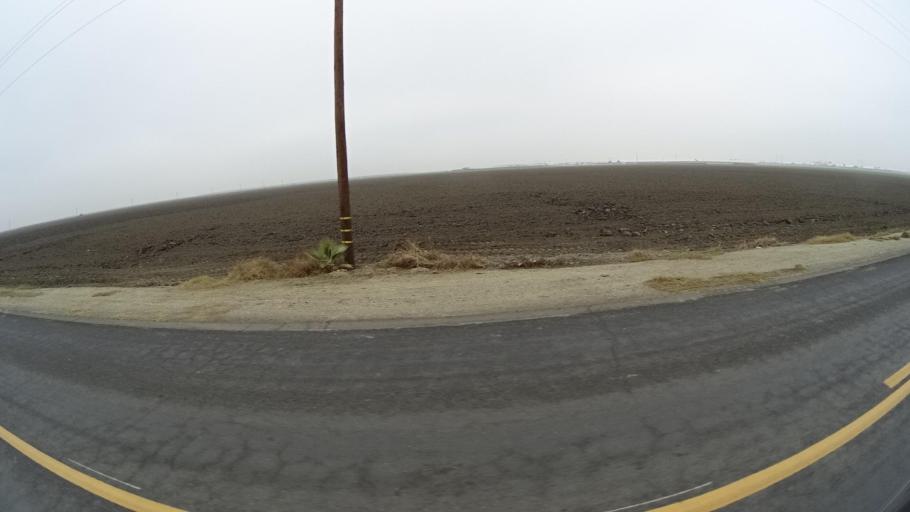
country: US
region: California
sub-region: Kern County
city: Greenfield
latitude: 35.1801
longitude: -119.1209
